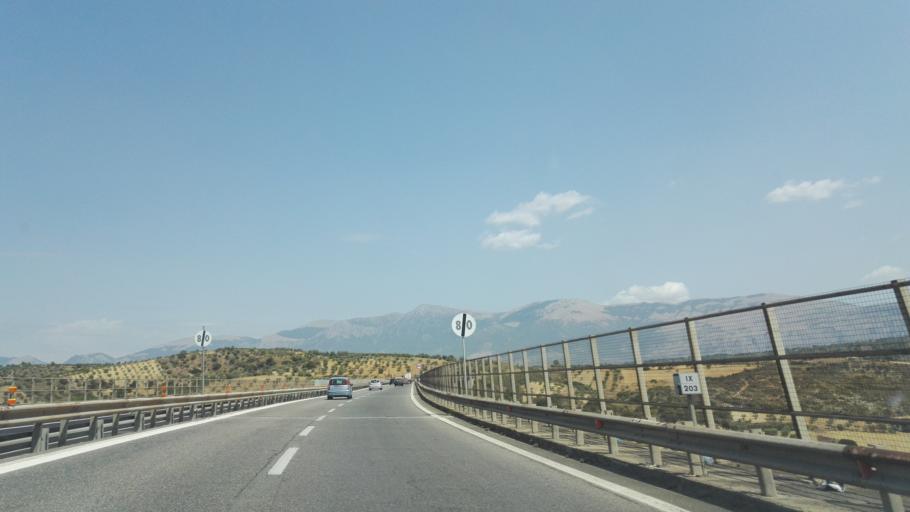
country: IT
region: Calabria
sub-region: Provincia di Cosenza
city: Castrovillari
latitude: 39.7563
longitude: 16.2207
